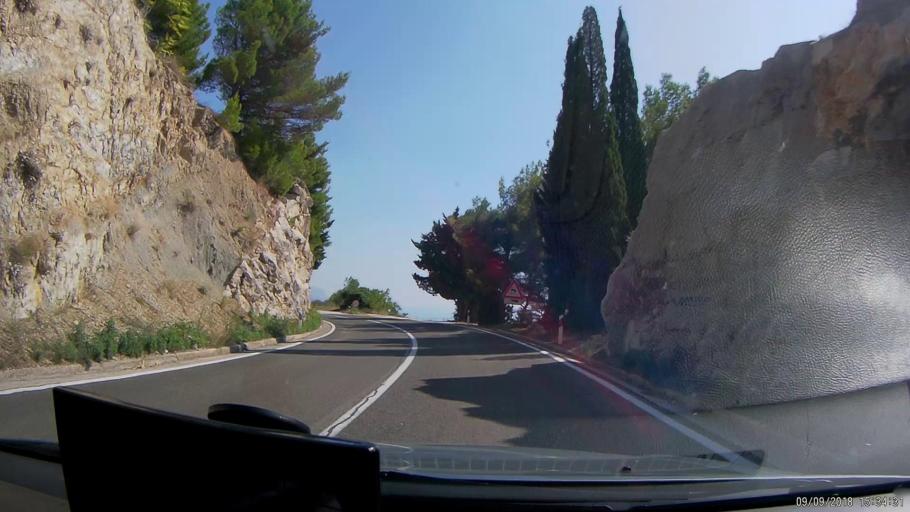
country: HR
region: Splitsko-Dalmatinska
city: Donja Brela
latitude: 43.3881
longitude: 16.9057
